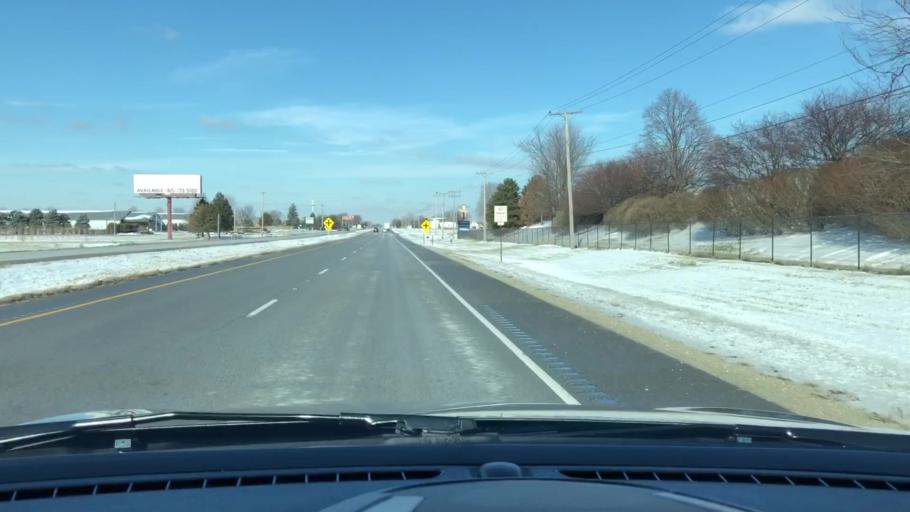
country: US
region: Illinois
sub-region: Will County
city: Preston Heights
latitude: 41.4641
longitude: -88.0795
